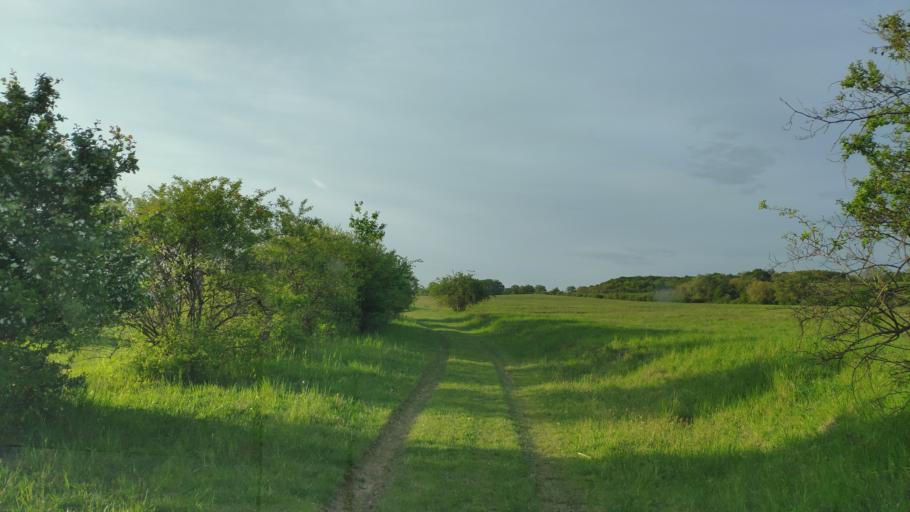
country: SK
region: Kosicky
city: Kosice
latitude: 48.7189
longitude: 21.3554
